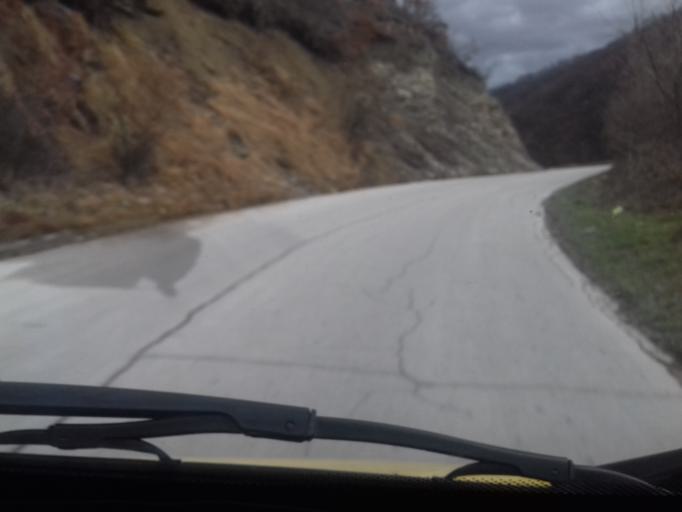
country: BA
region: Federation of Bosnia and Herzegovina
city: Zenica
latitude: 44.2266
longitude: 17.9750
